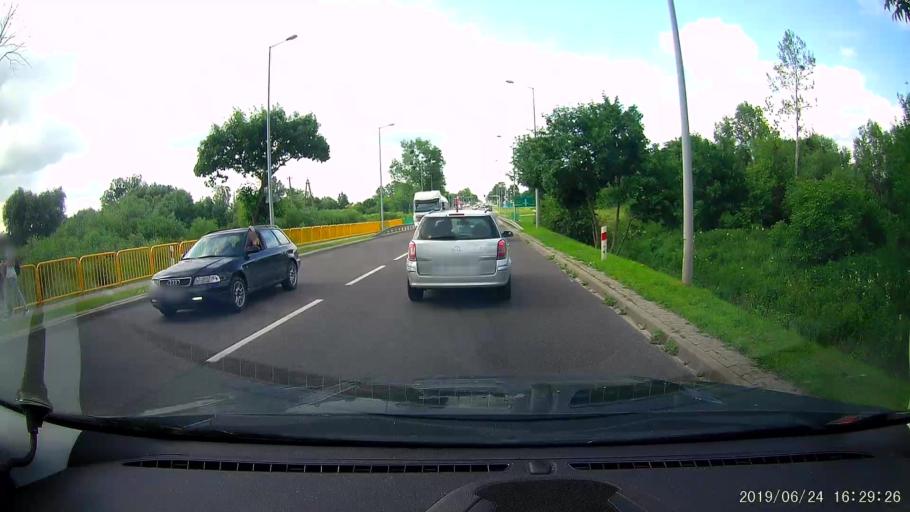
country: PL
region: Lublin Voivodeship
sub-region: Powiat tomaszowski
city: Tomaszow Lubelski
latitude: 50.4591
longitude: 23.4208
